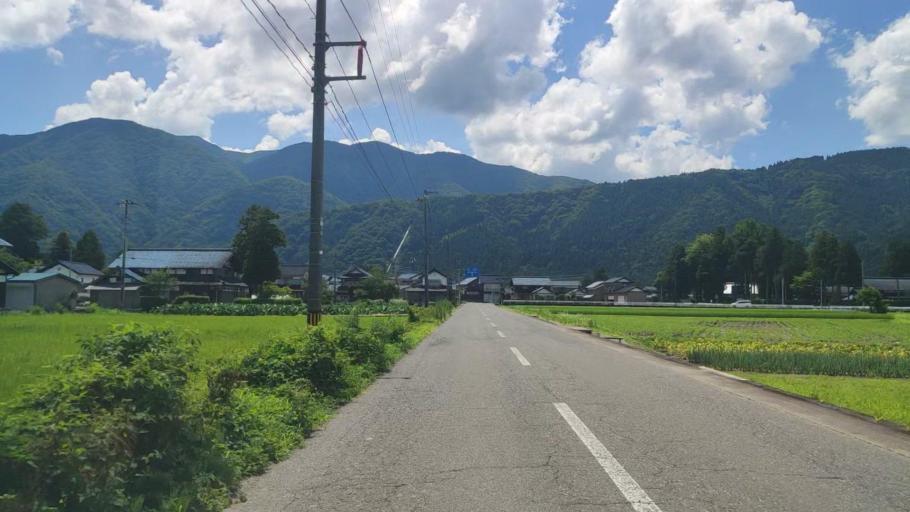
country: JP
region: Fukui
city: Ono
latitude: 35.9444
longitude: 136.5446
